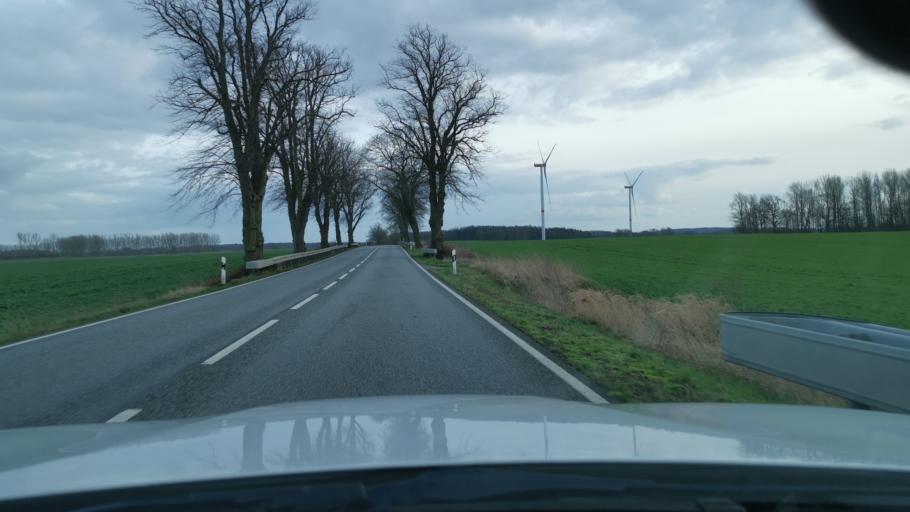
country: DE
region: Mecklenburg-Vorpommern
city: Dummerstorf
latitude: 54.0139
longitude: 12.2494
